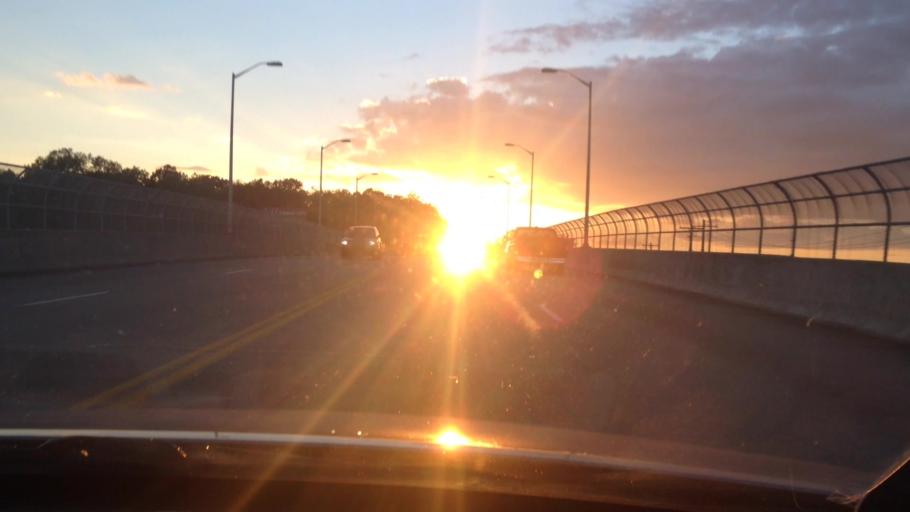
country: US
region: Missouri
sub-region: Jackson County
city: Raytown
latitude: 39.0346
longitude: -94.5255
